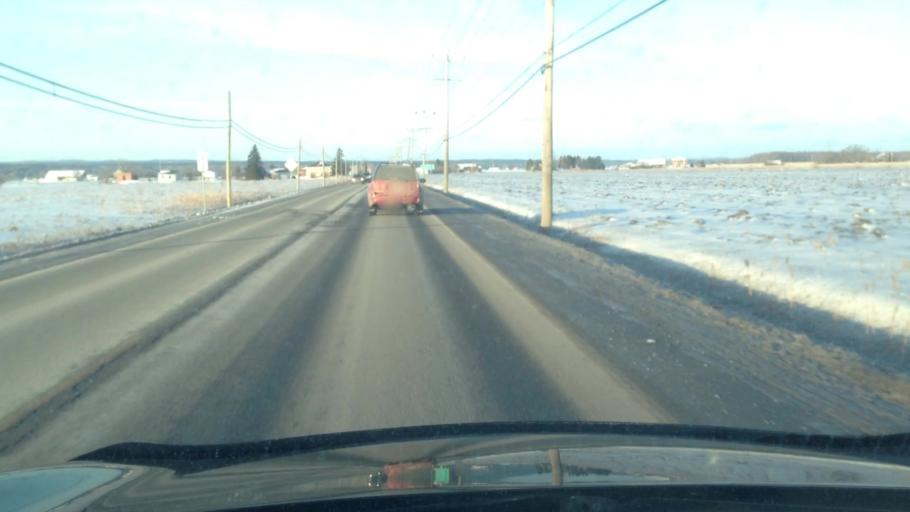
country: CA
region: Quebec
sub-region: Lanaudiere
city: Saint-Lin-Laurentides
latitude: 45.8707
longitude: -73.7572
